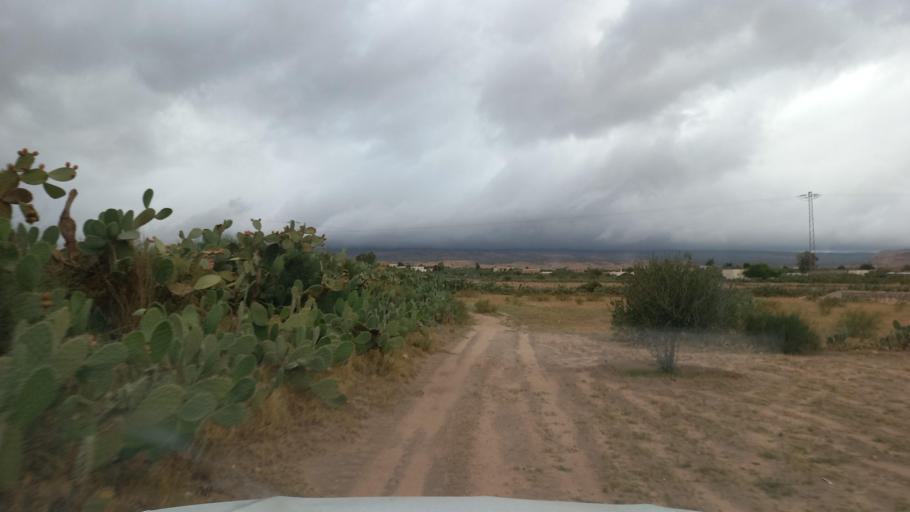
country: TN
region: Al Qasrayn
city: Kasserine
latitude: 35.2765
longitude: 8.9470
